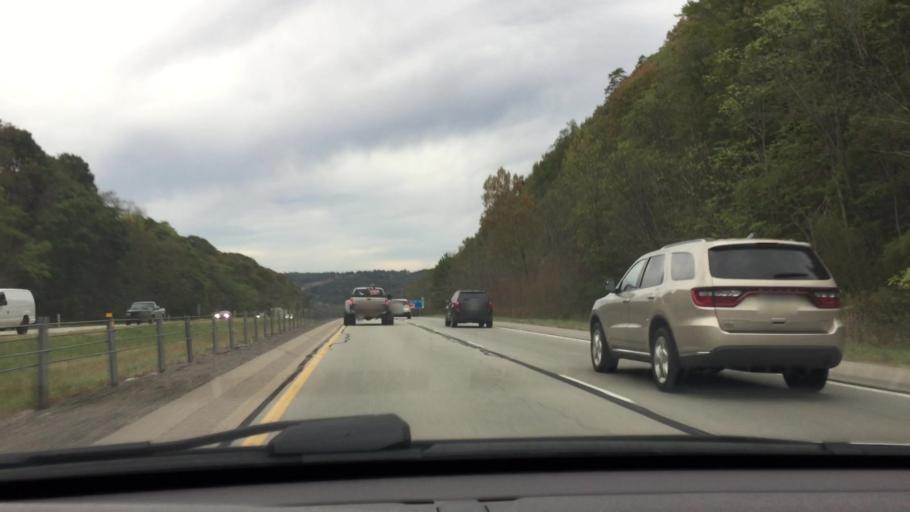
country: US
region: Pennsylvania
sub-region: Beaver County
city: Ambridge
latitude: 40.5897
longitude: -80.2940
